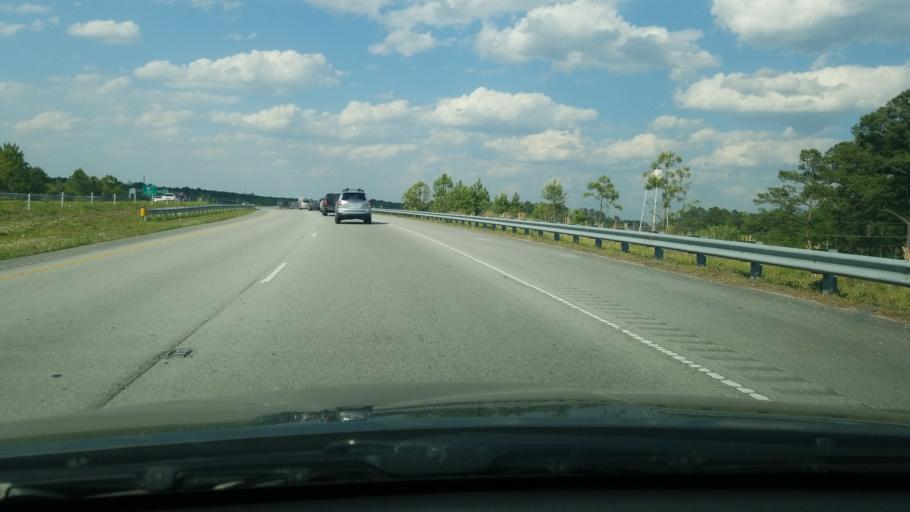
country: US
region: North Carolina
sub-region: Onslow County
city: Jacksonville
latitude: 34.7536
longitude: -77.3961
